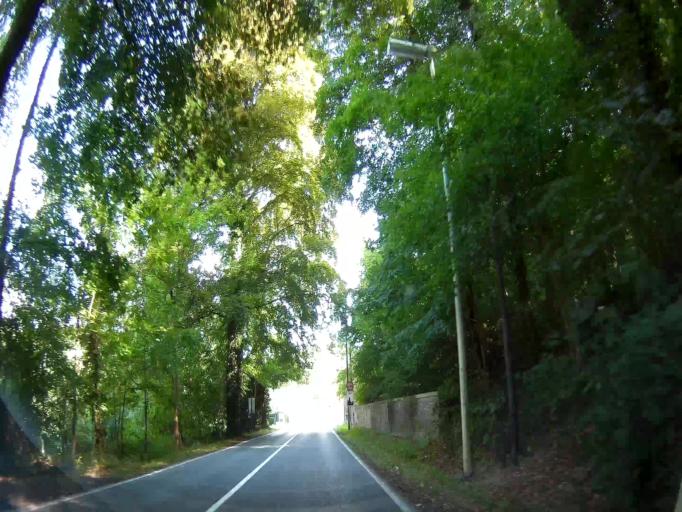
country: BE
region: Wallonia
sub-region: Province de Namur
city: Yvoir
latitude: 50.3371
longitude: 4.8643
